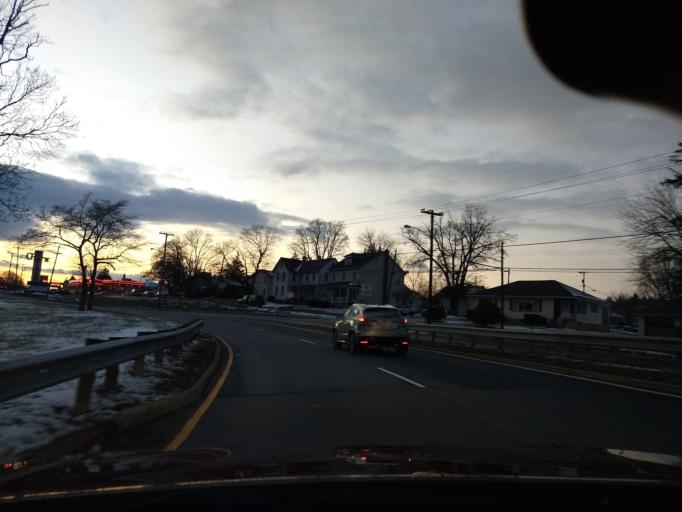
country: US
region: New Jersey
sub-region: Warren County
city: Phillipsburg
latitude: 40.6993
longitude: -75.1650
